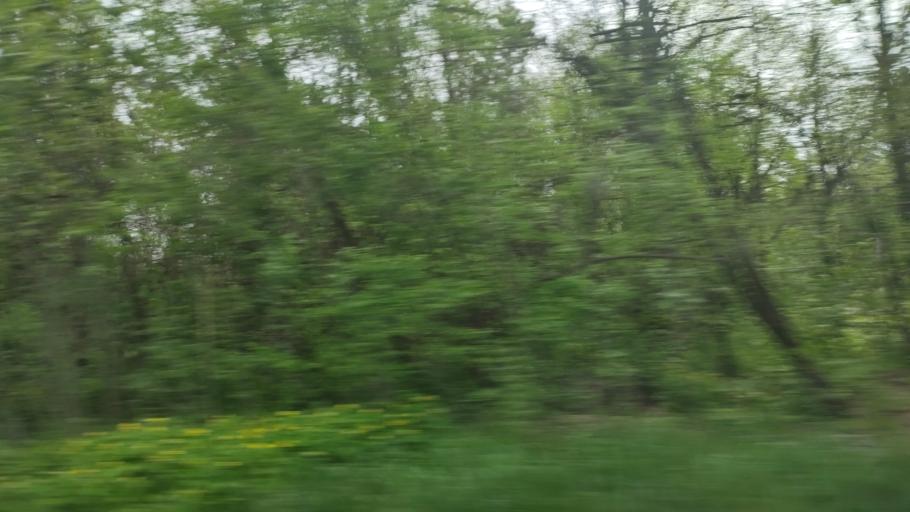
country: RO
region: Constanta
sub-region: Oras Murfatlar
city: Murfatlar
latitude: 44.1681
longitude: 28.3949
